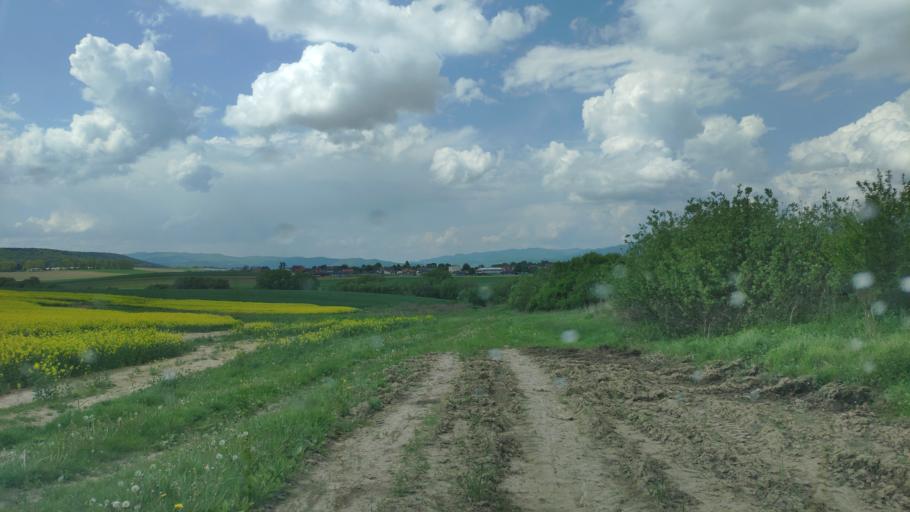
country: SK
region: Presovsky
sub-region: Okres Presov
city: Presov
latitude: 49.0323
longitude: 21.1651
